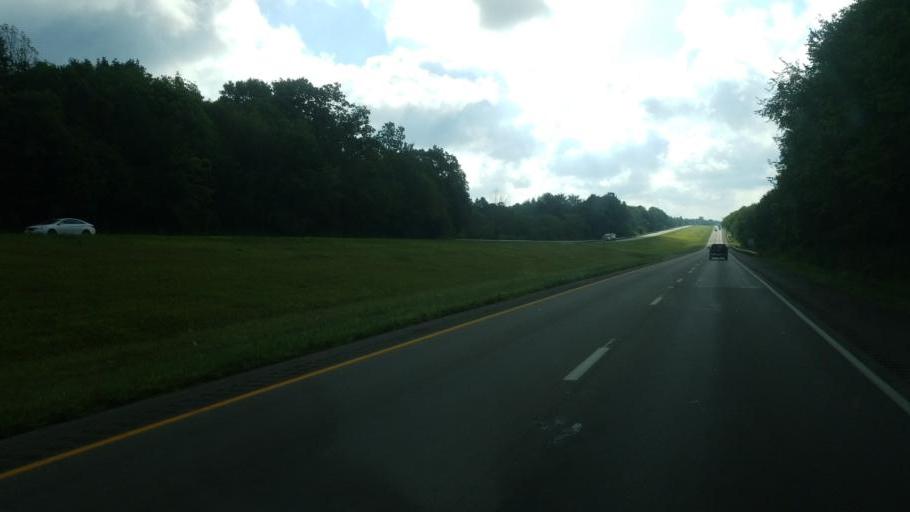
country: US
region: Ohio
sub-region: Stark County
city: Massillon
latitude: 40.7643
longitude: -81.5732
